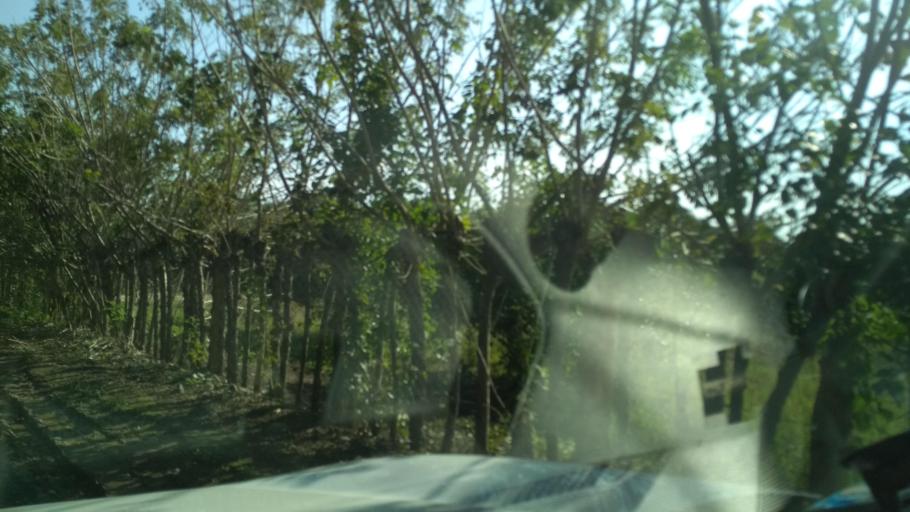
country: MX
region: Veracruz
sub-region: Martinez de la Torre
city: El Progreso
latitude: 20.0864
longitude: -97.0202
